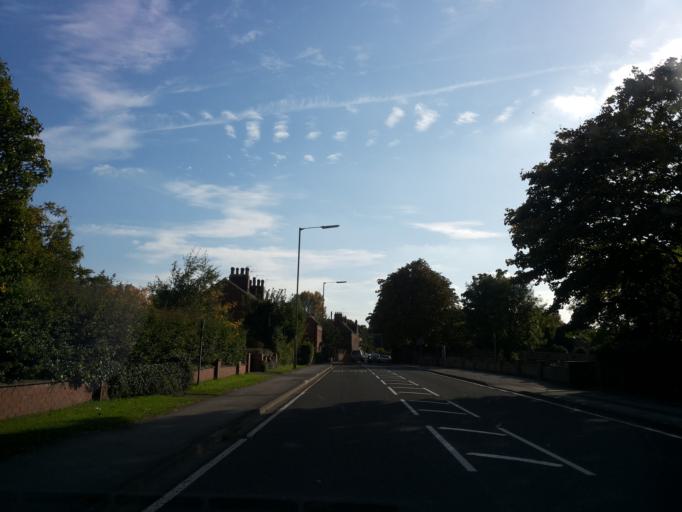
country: GB
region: England
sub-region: North Yorkshire
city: Camblesforth
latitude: 53.7116
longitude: -1.0196
